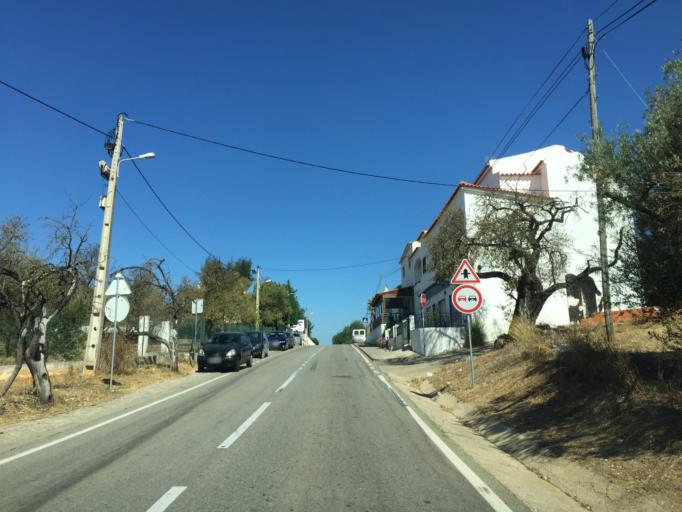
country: PT
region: Faro
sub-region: Loule
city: Vilamoura
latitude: 37.1172
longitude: -8.0937
